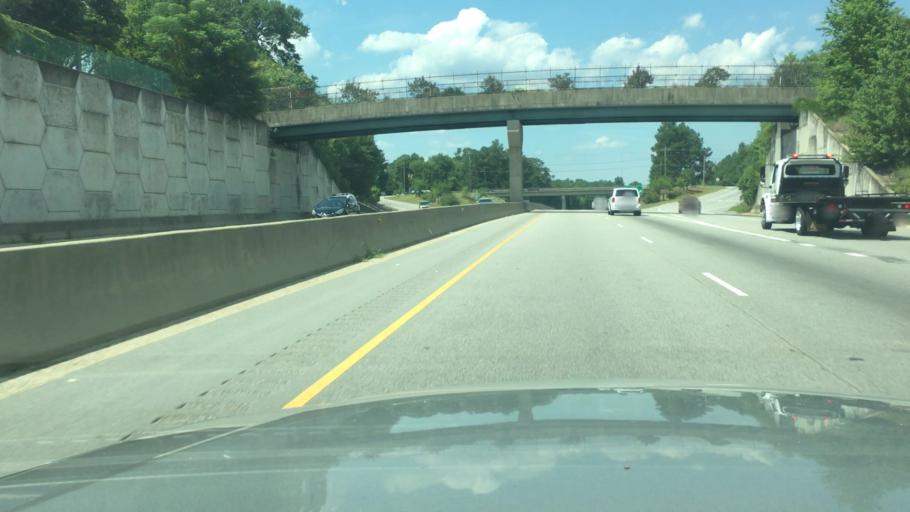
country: US
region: North Carolina
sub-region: Cumberland County
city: Fayetteville
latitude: 35.0536
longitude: -78.8938
